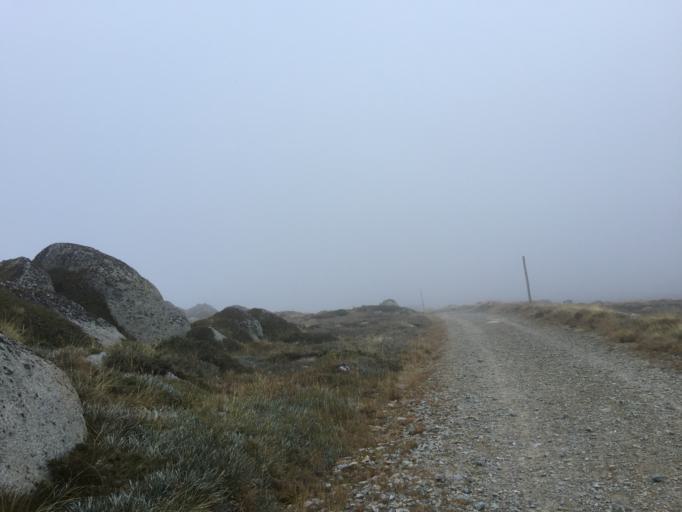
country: AU
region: New South Wales
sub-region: Snowy River
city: Jindabyne
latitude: -36.4530
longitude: 148.2871
